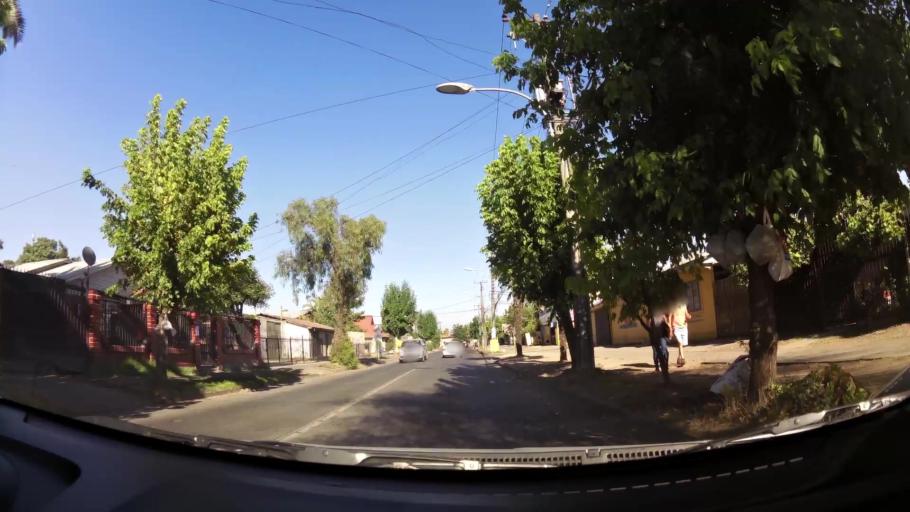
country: CL
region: Maule
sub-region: Provincia de Curico
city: Curico
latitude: -34.9877
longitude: -71.2504
